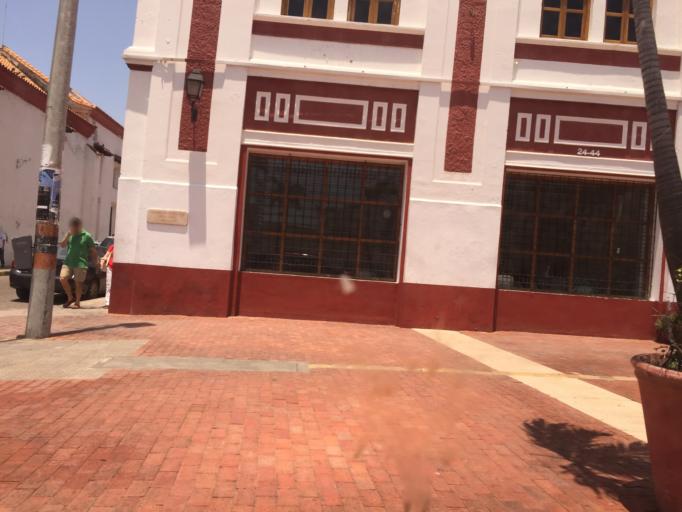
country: CO
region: Bolivar
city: Cartagena
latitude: 10.4211
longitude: -75.5484
